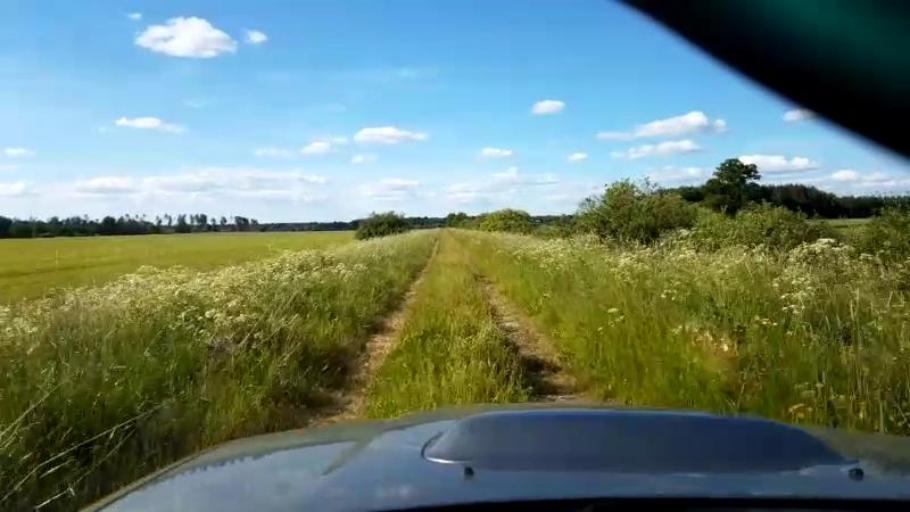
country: EE
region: Paernumaa
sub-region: Sauga vald
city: Sauga
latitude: 58.4982
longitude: 24.5913
